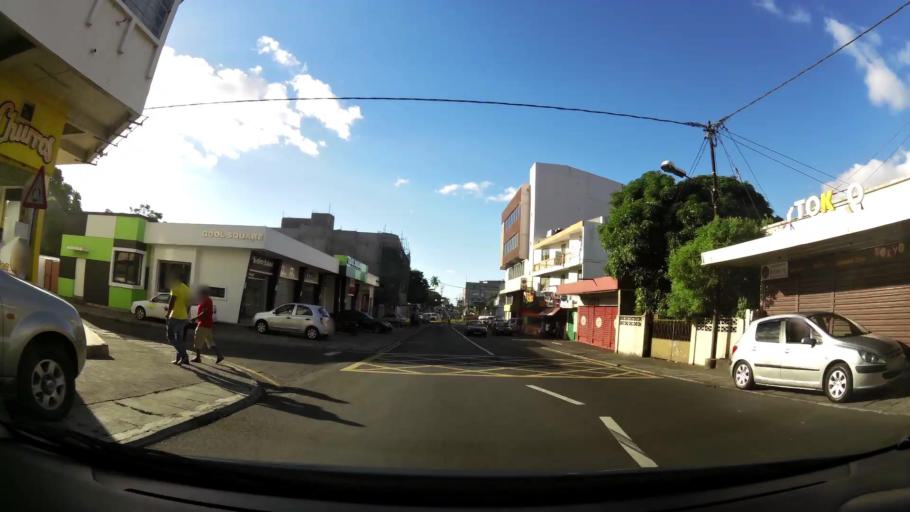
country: MU
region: Plaines Wilhems
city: Ebene
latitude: -20.2280
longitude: 57.4677
